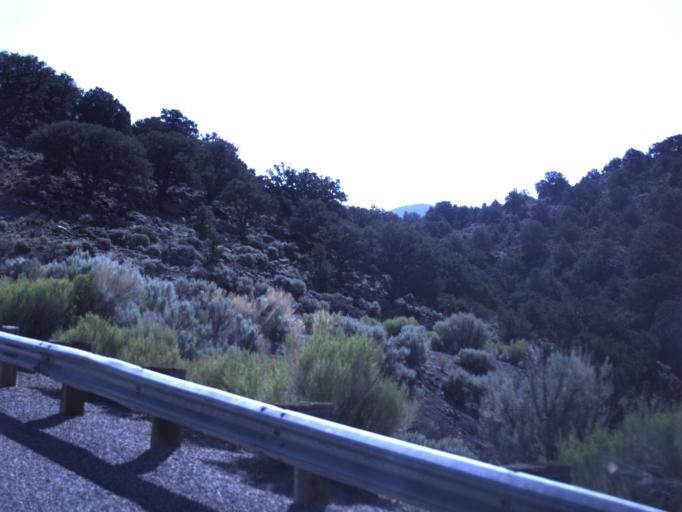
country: US
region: Utah
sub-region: Wayne County
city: Loa
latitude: 38.4791
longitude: -111.5528
